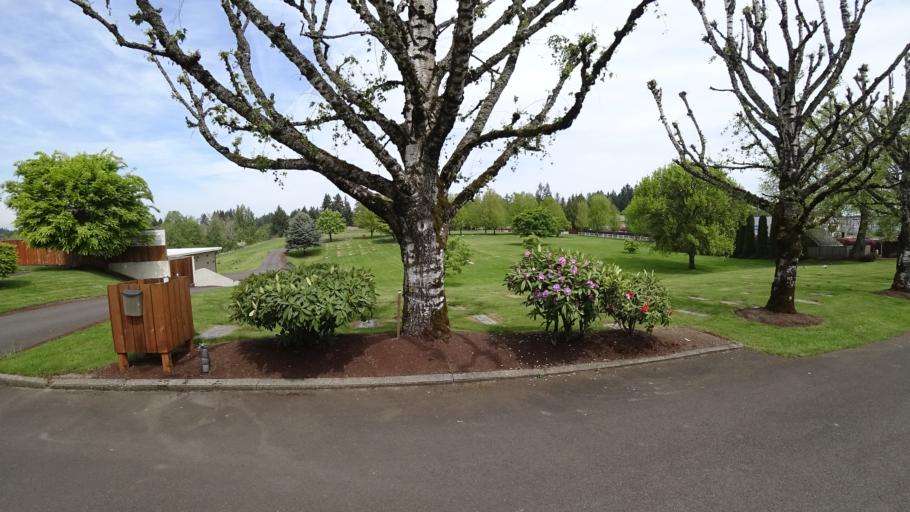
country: US
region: Oregon
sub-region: Washington County
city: Hillsboro
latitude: 45.5023
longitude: -122.9429
